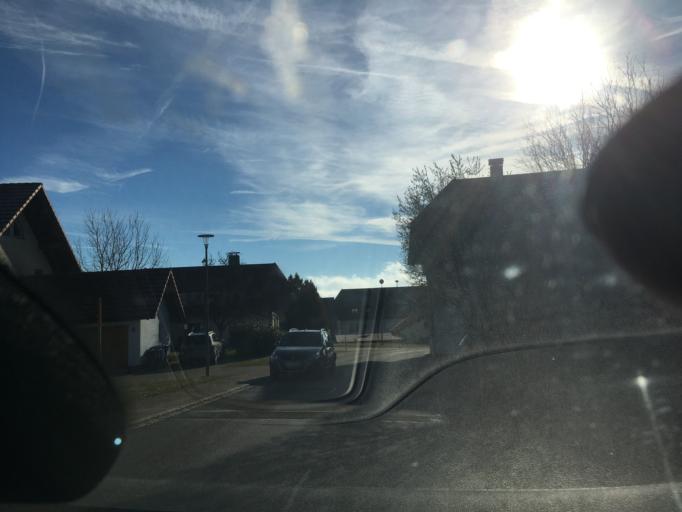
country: DE
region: Baden-Wuerttemberg
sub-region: Freiburg Region
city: Gorwihl
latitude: 47.6464
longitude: 8.0617
